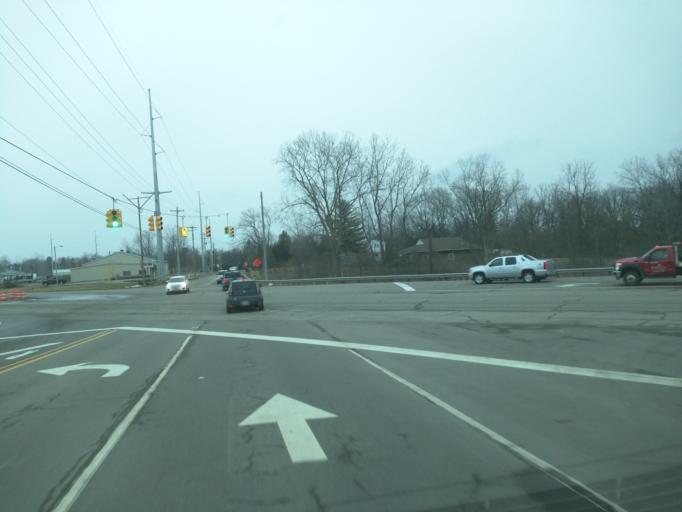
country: US
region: Michigan
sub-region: Eaton County
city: Waverly
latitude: 42.7120
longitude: -84.6101
